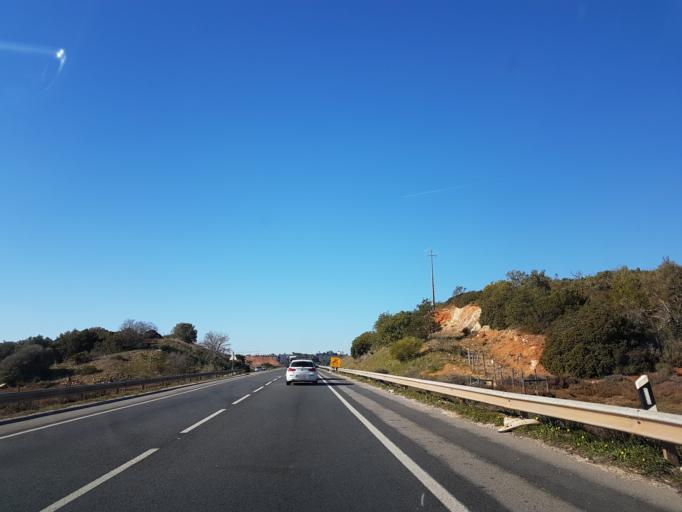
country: PT
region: Faro
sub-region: Portimao
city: Portimao
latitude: 37.1519
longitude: -8.5132
